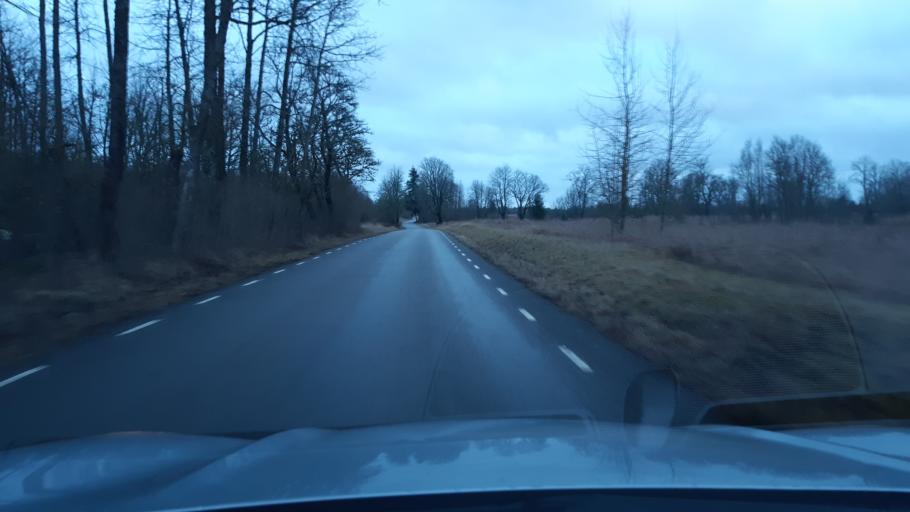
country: EE
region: Raplamaa
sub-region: Rapla vald
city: Rapla
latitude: 58.9950
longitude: 24.7208
